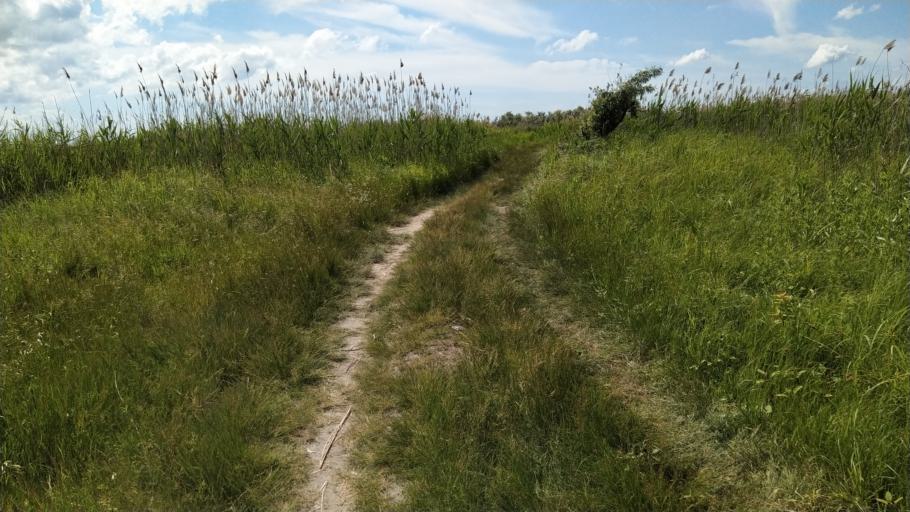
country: RU
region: Rostov
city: Bataysk
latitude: 47.1356
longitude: 39.6718
